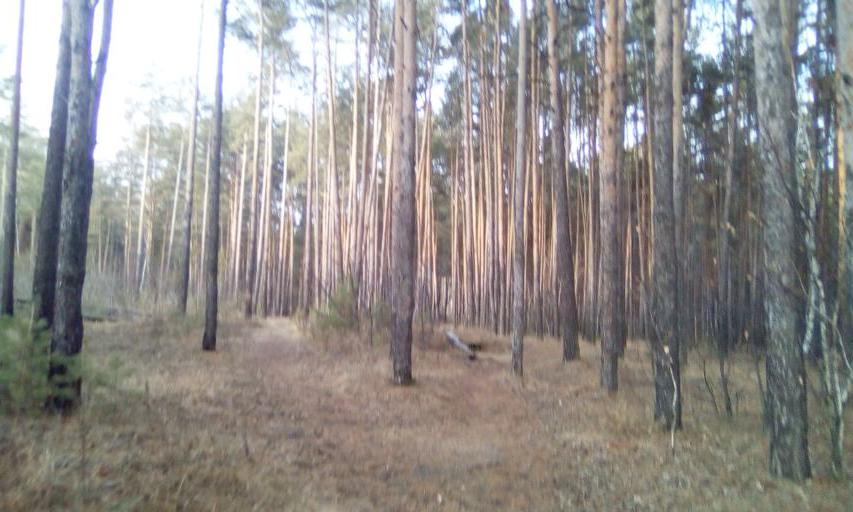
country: RU
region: Chelyabinsk
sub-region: Gorod Chelyabinsk
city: Chelyabinsk
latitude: 55.1632
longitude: 61.3528
